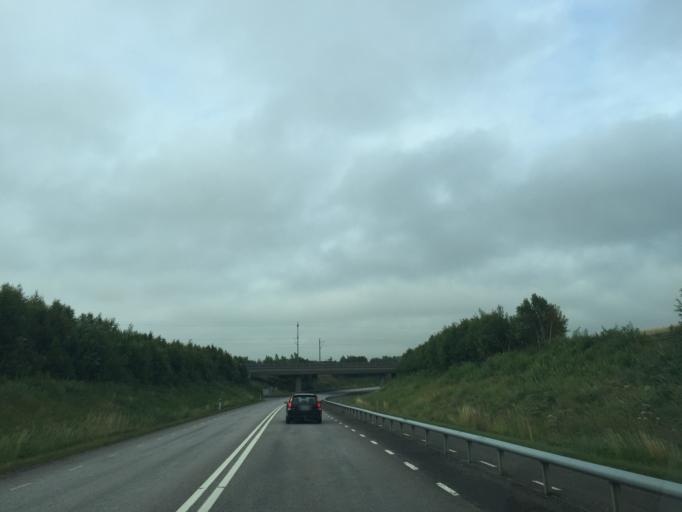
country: SE
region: Halland
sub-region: Falkenbergs Kommun
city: Falkenberg
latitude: 56.8838
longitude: 12.5965
